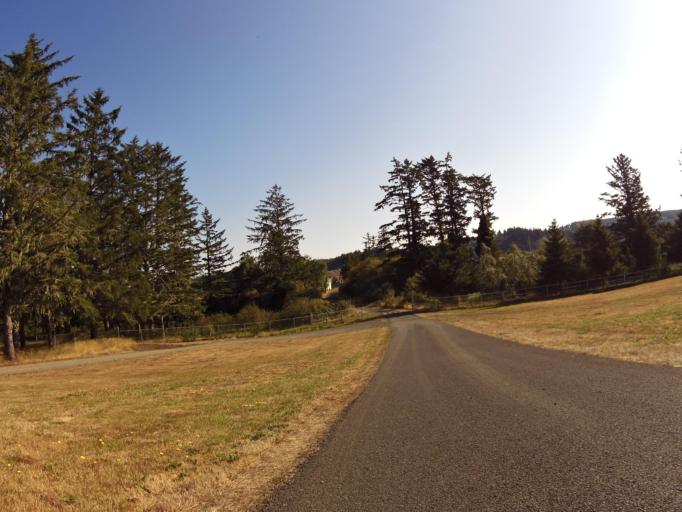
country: US
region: Oregon
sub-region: Clatsop County
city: Warrenton
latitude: 46.1174
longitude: -123.9283
